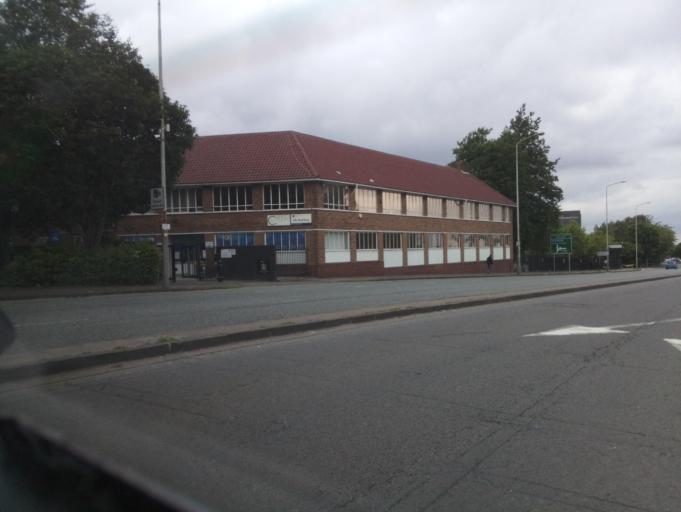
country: GB
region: England
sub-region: Wolverhampton
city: Wolverhampton
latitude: 52.5903
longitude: -2.1262
